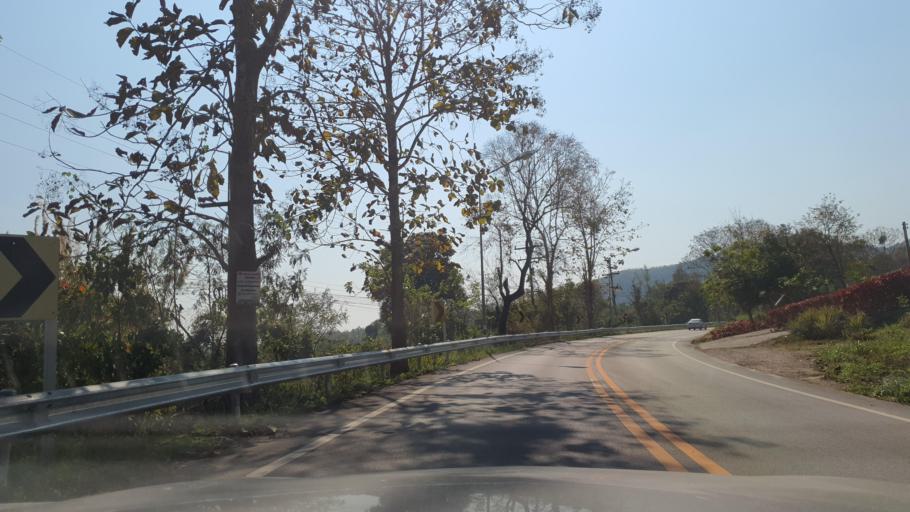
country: TH
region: Chiang Rai
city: Mae Lao
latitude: 19.8327
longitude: 99.6893
